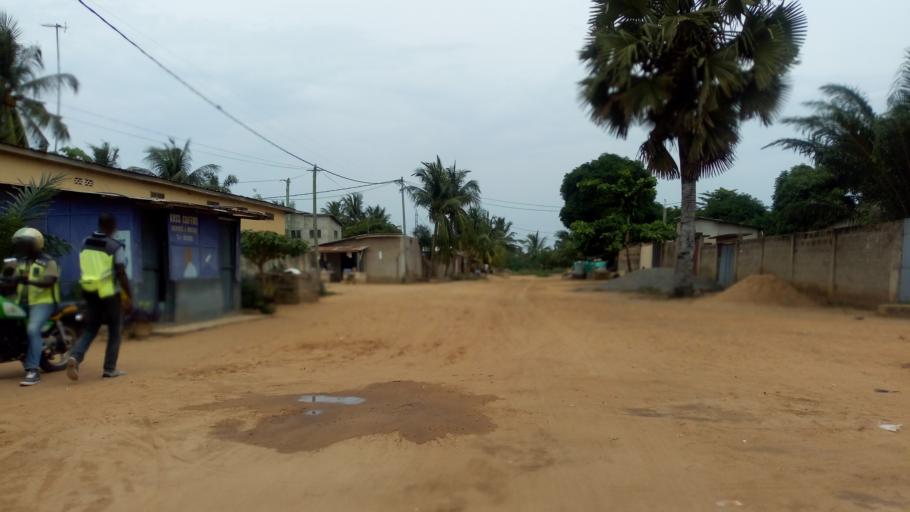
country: TG
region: Maritime
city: Lome
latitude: 6.1715
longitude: 1.1772
